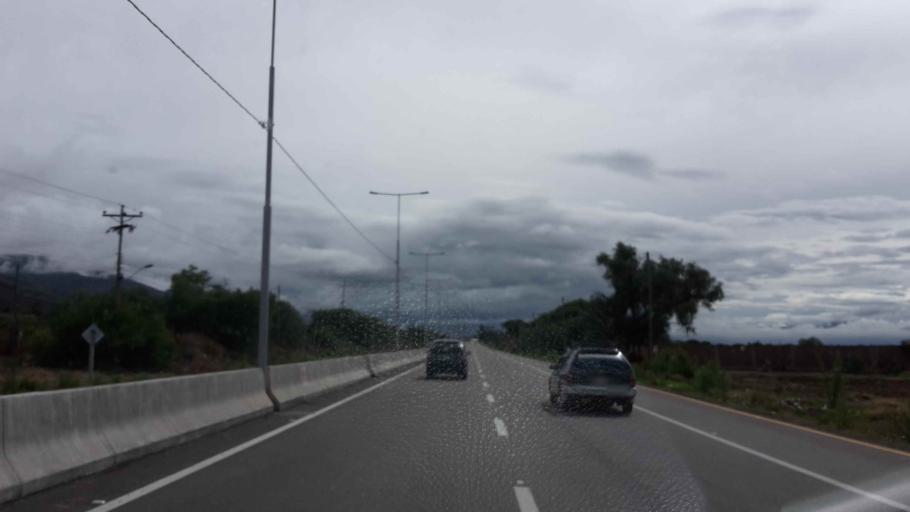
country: BO
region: Cochabamba
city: Tarata
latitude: -17.5440
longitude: -66.0038
